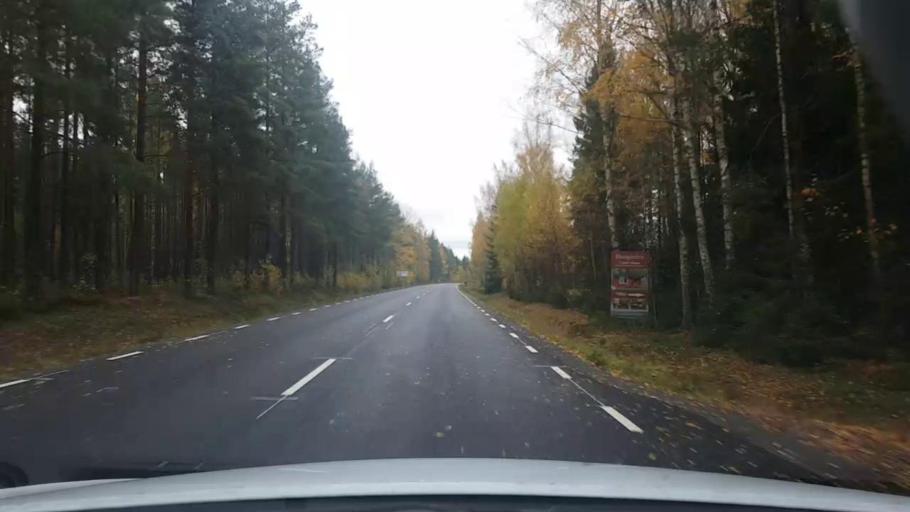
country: SE
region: OErebro
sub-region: Laxa Kommun
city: Laxa
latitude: 58.7964
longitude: 14.5422
